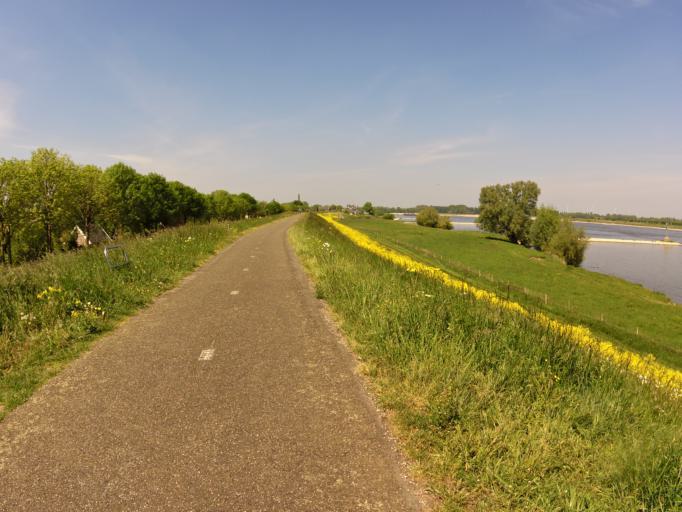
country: NL
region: Gelderland
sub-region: Gemeente Neerijnen
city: Neerijnen
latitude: 51.8111
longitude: 5.3278
